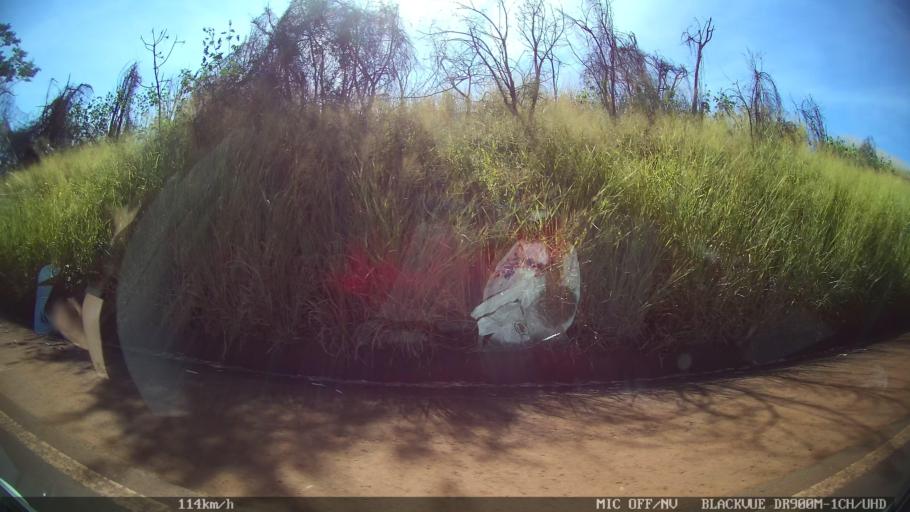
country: BR
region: Sao Paulo
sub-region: Sao Joaquim Da Barra
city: Sao Joaquim da Barra
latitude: -20.5501
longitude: -47.7479
